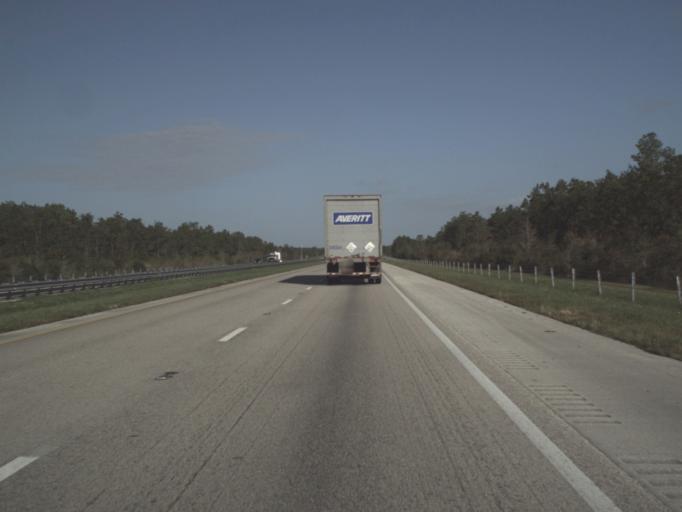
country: US
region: Florida
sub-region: Osceola County
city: Saint Cloud
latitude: 27.9747
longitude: -81.1129
